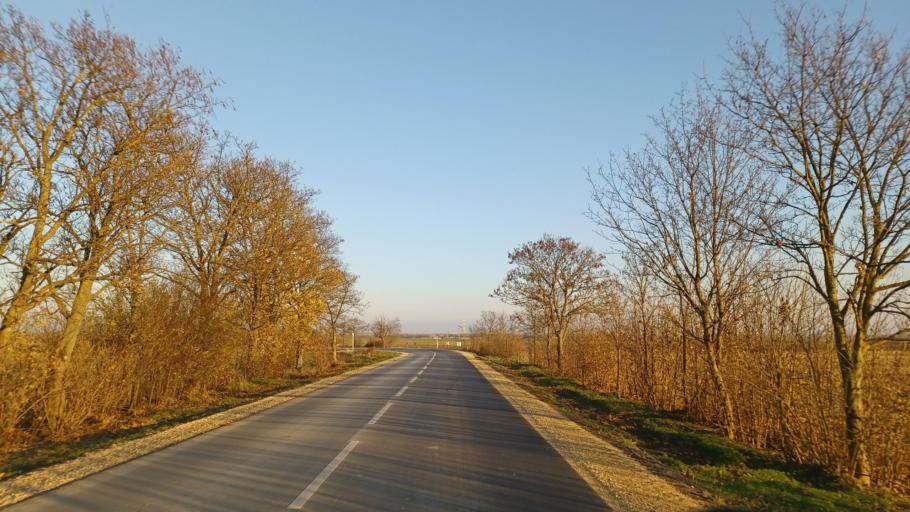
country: HU
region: Tolna
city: Fadd
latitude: 46.4842
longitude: 18.8717
